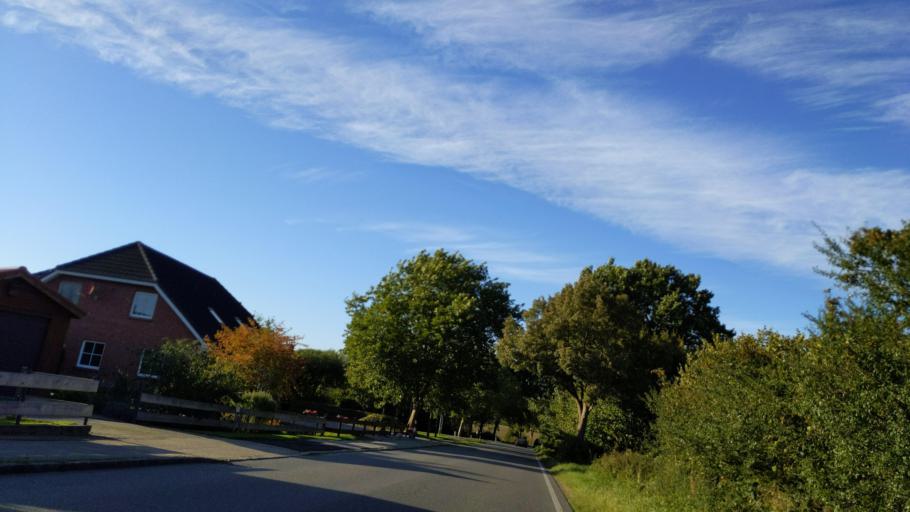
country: DE
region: Schleswig-Holstein
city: Ahrensbok
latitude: 54.0199
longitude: 10.5692
